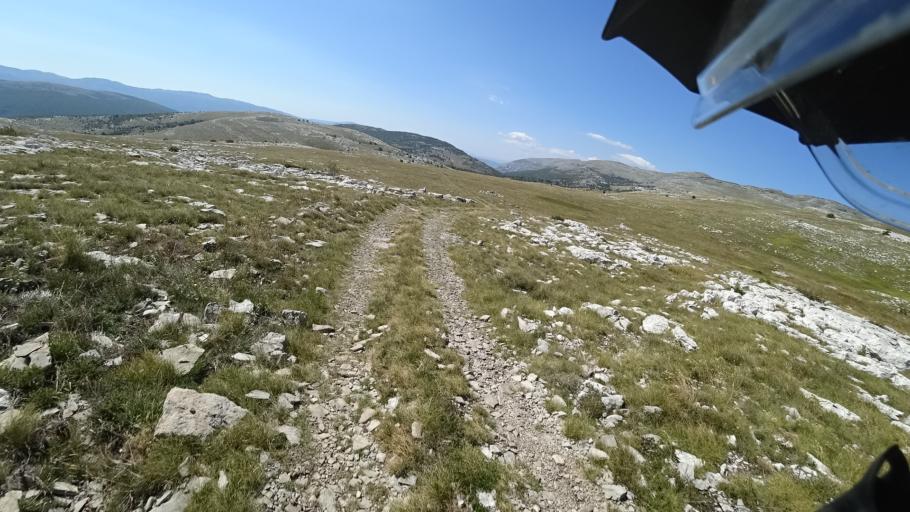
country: HR
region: Splitsko-Dalmatinska
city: Hrvace
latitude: 43.9016
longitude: 16.6037
